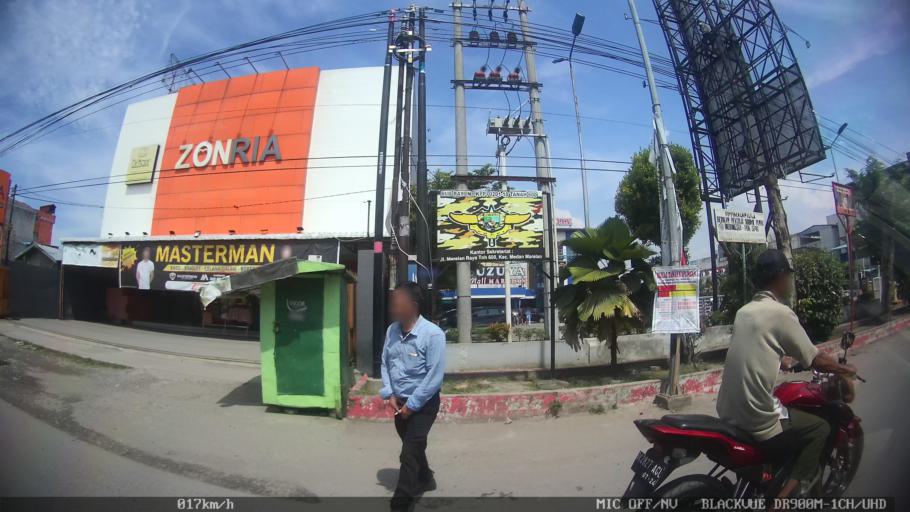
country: ID
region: North Sumatra
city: Labuhan Deli
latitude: 3.6788
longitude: 98.6560
